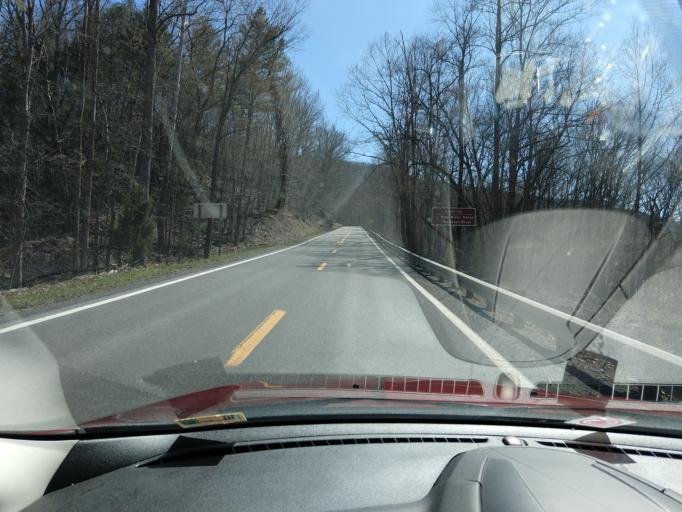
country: US
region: West Virginia
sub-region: Summers County
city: Hinton
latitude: 37.7683
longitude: -80.8920
